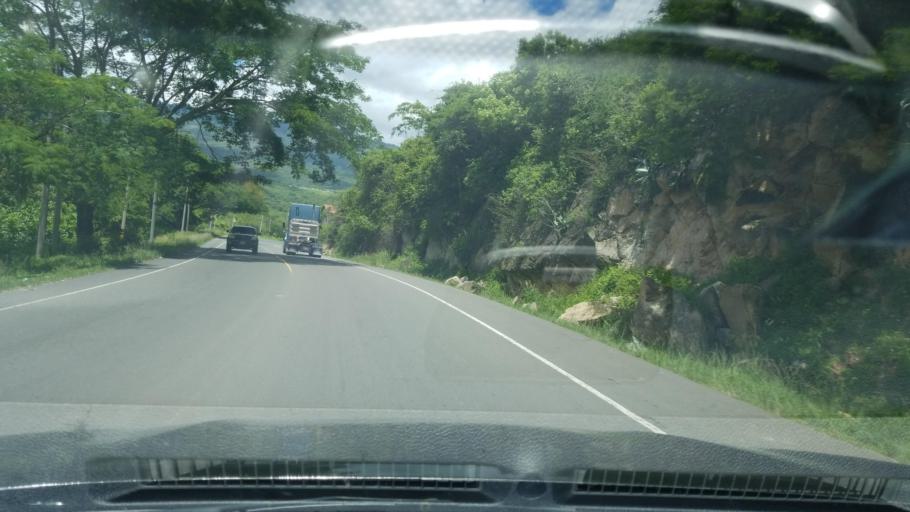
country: HN
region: Francisco Morazan
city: Rio Abajo
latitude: 14.1782
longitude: -87.2050
